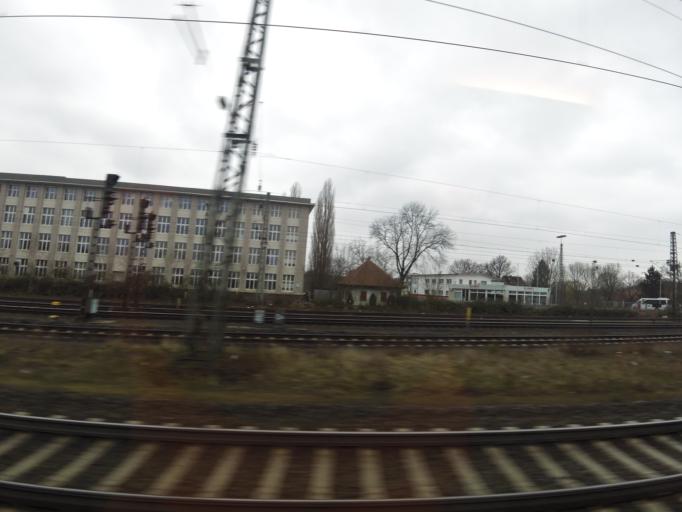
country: DE
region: North Rhine-Westphalia
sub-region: Regierungsbezirk Detmold
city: Minden
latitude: 52.2872
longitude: 8.9331
